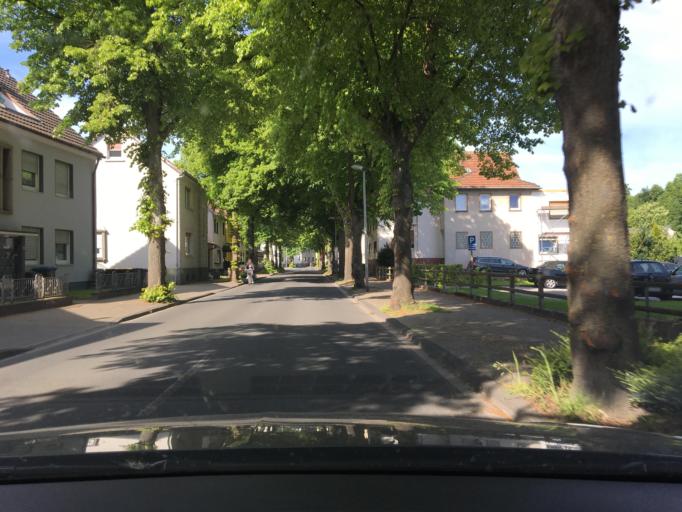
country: DE
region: North Rhine-Westphalia
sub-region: Regierungsbezirk Arnsberg
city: Frondenberg
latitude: 51.4744
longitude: 7.7840
